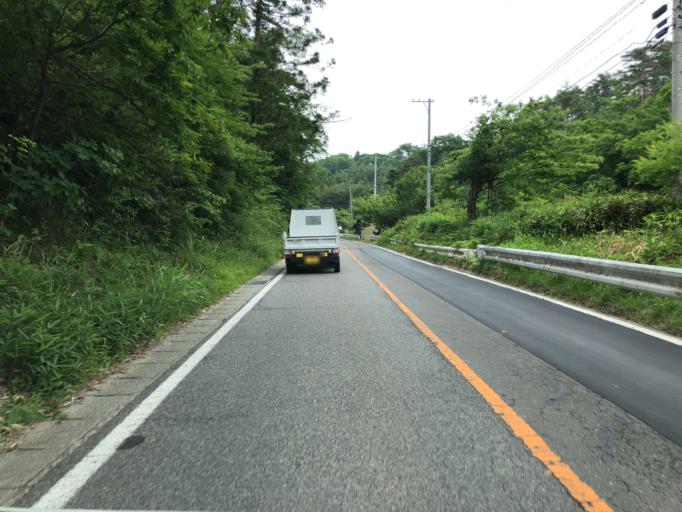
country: JP
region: Fukushima
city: Funehikimachi-funehiki
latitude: 37.5322
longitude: 140.5499
